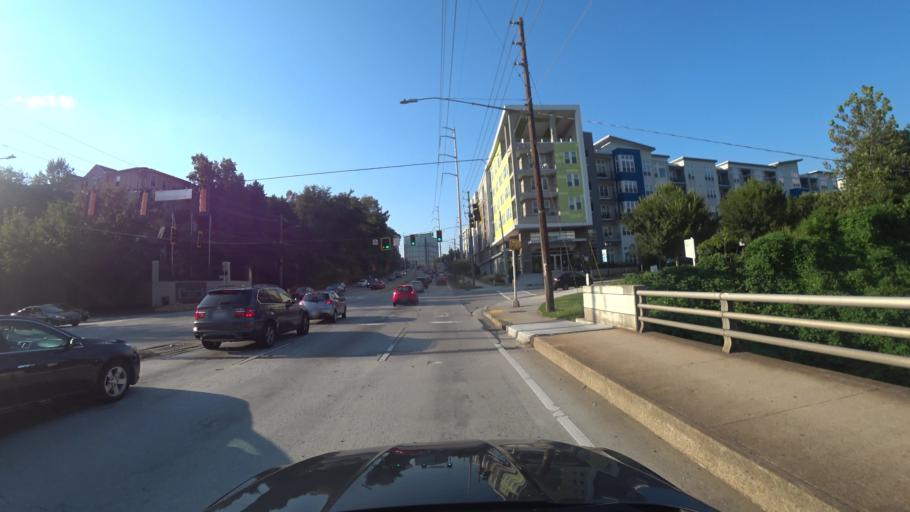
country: US
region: Georgia
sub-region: DeKalb County
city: Druid Hills
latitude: 33.8174
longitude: -84.3668
